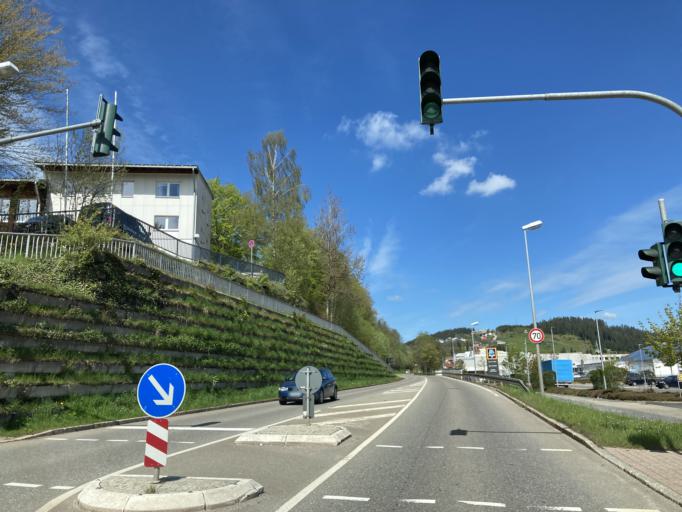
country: DE
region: Baden-Wuerttemberg
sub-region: Freiburg Region
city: Furtwangen im Schwarzwald
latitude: 48.0474
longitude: 8.2149
